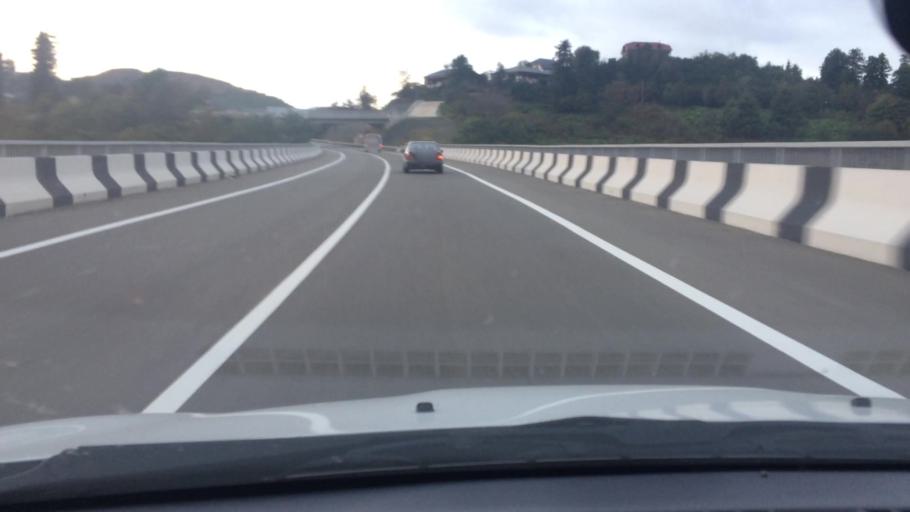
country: GE
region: Ajaria
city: Makhinjauri
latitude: 41.7167
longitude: 41.7518
